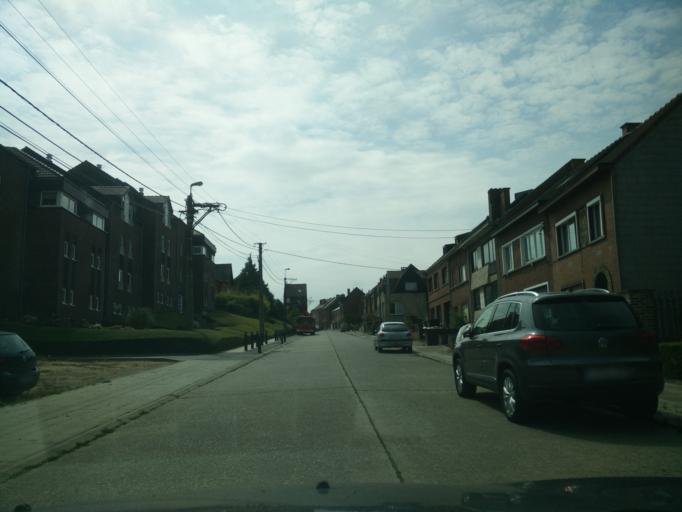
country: BE
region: Wallonia
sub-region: Province du Brabant Wallon
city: Tubize
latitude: 50.6926
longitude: 4.2214
